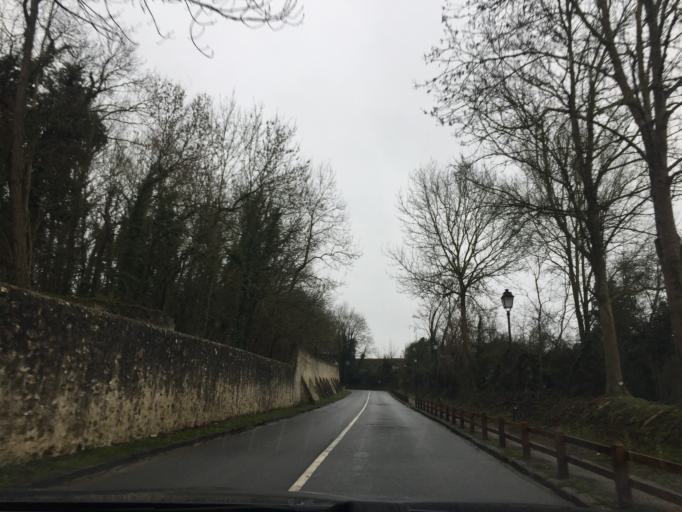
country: FR
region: Ile-de-France
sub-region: Departement de Seine-et-Marne
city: Coupvray
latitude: 48.8891
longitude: 2.7925
